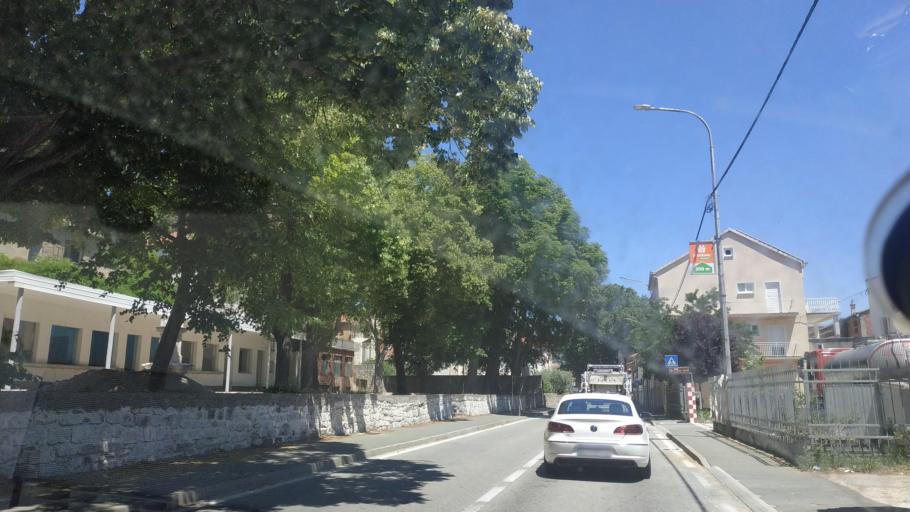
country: HR
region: Sibensko-Kniniska
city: Knin
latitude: 44.0319
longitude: 16.1937
